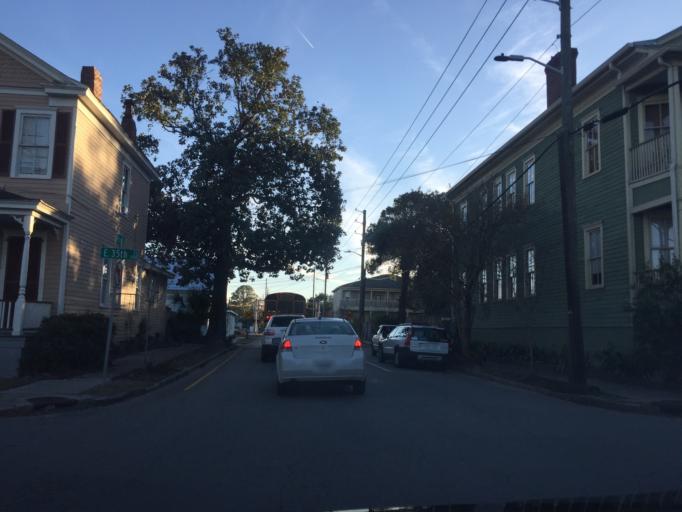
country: US
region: Georgia
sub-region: Chatham County
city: Savannah
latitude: 32.0577
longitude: -81.0940
